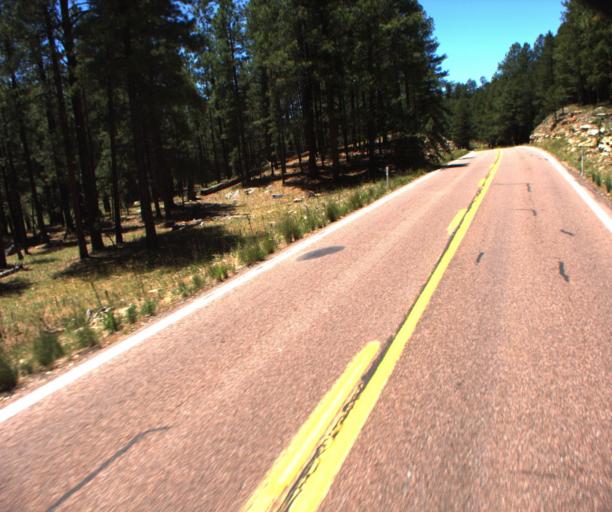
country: US
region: Arizona
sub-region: Gila County
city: Pine
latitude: 34.5366
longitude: -111.3357
